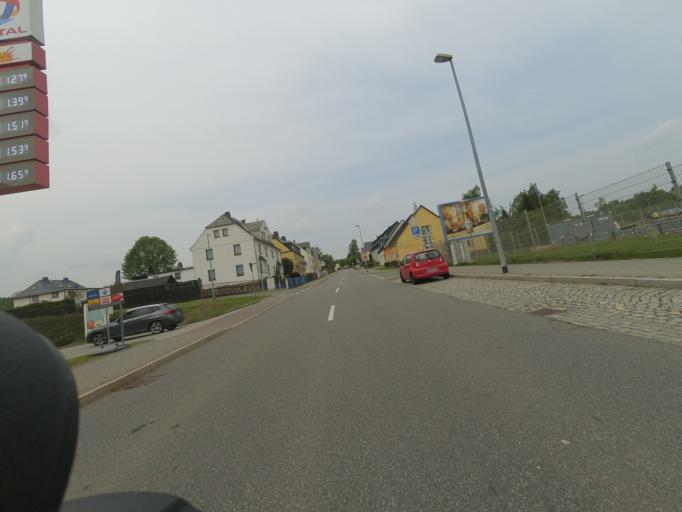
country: DE
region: Saxony
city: Marienberg
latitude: 50.6500
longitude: 13.1564
